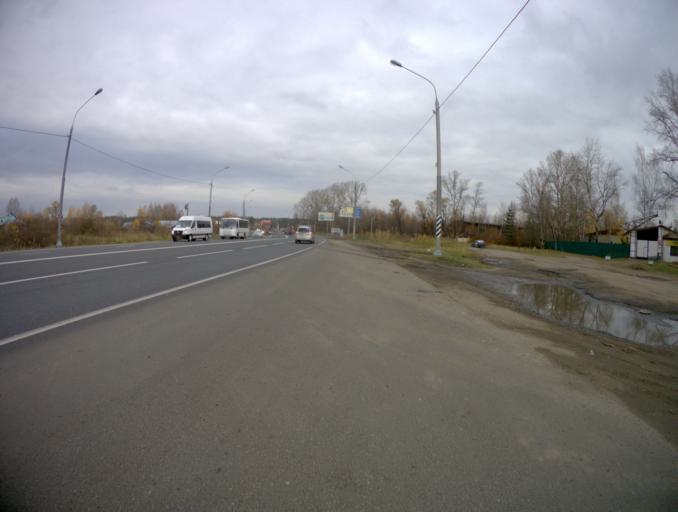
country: RU
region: Moskovskaya
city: Orekhovo-Zuyevo
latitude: 55.8403
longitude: 38.9700
